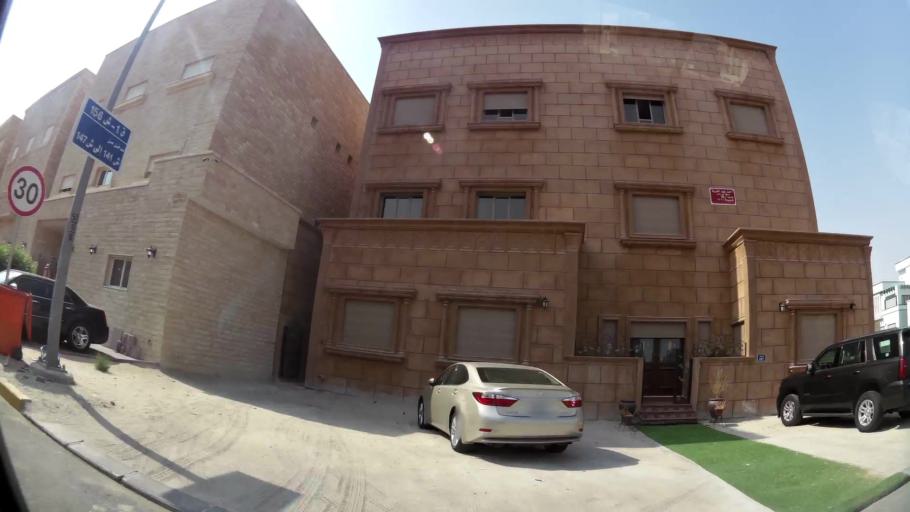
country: KW
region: Muhafazat al Jahra'
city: Al Jahra'
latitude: 29.3330
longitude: 47.7794
